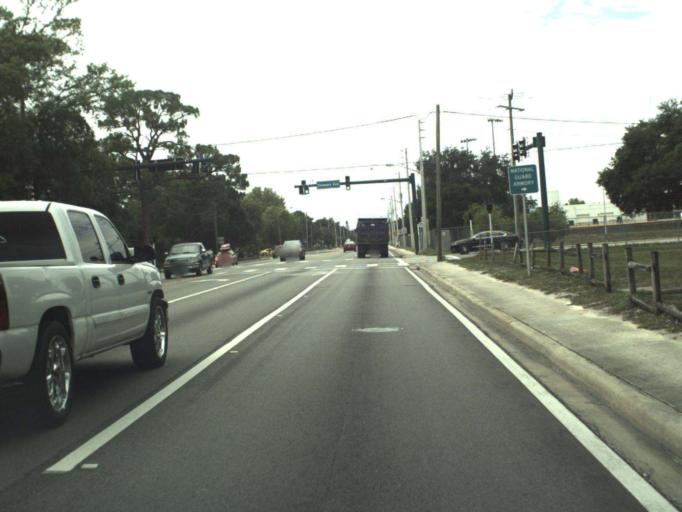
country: US
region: Florida
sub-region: Saint Lucie County
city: Fort Pierce
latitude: 27.4444
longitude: -80.3500
